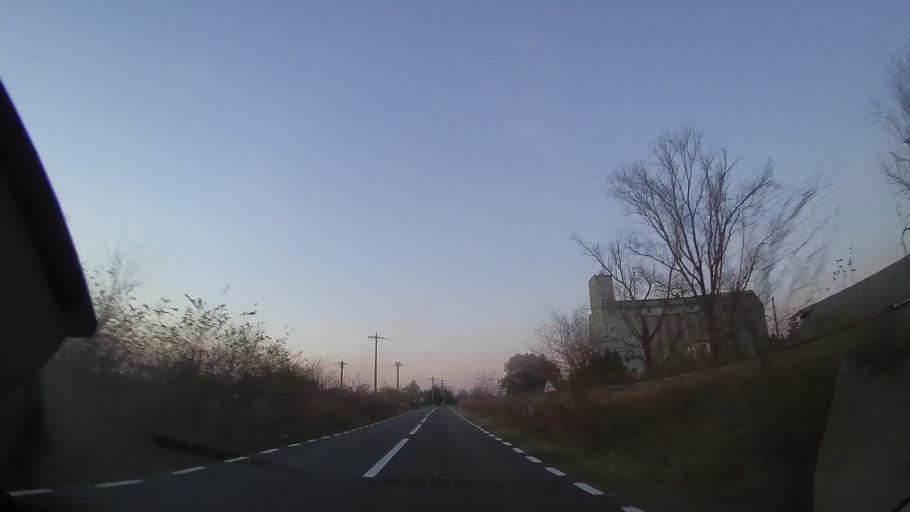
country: RO
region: Constanta
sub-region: Comuna Cobadin
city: Cobadin
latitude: 44.0508
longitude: 28.2486
